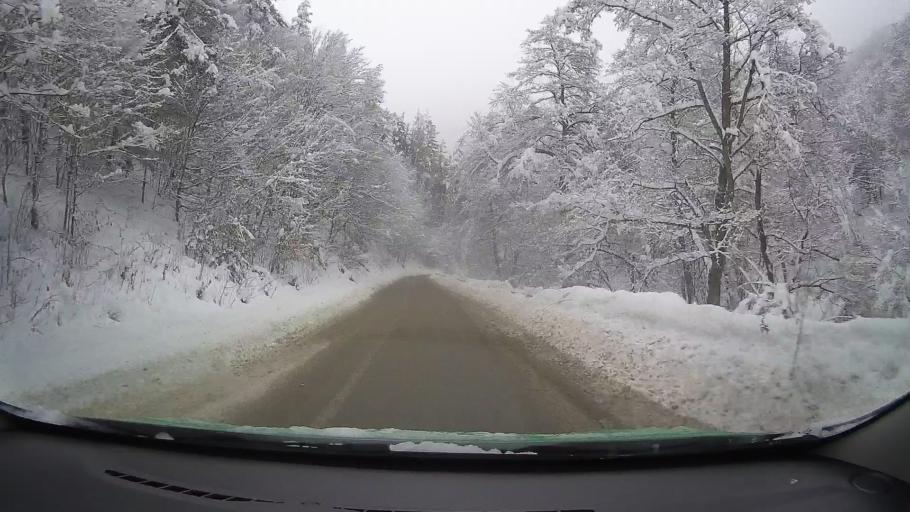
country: RO
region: Sibiu
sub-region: Comuna Tilisca
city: Tilisca
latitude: 45.7977
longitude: 23.8068
